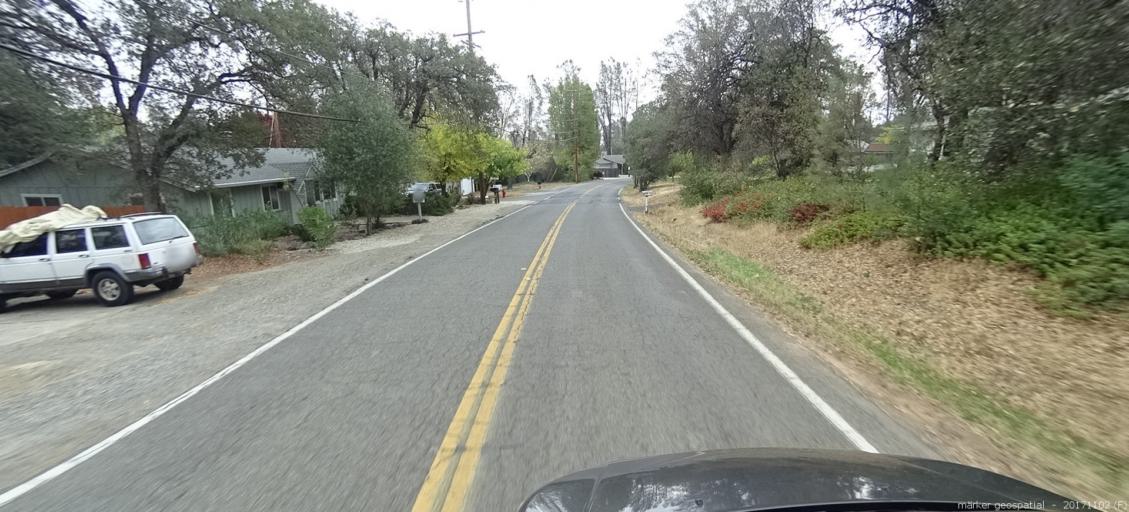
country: US
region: California
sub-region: Shasta County
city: Redding
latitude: 40.6342
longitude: -122.4094
